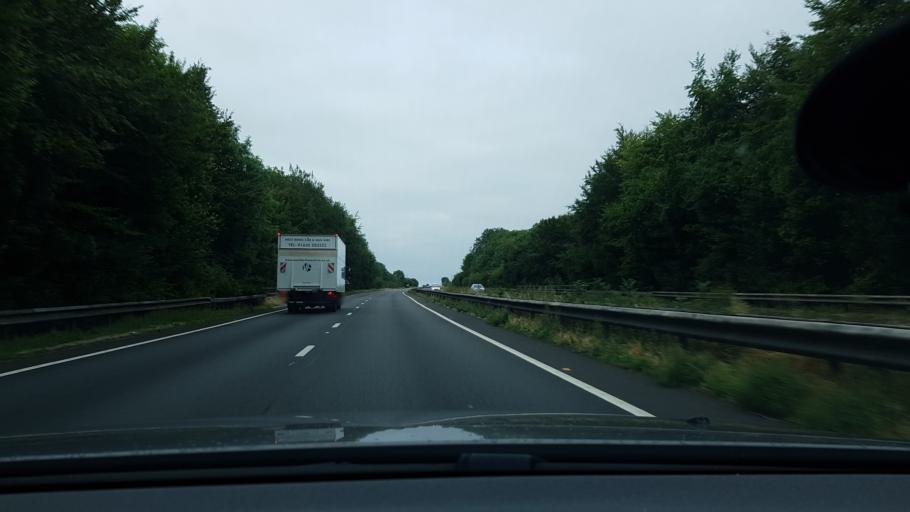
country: GB
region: England
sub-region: Hampshire
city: Overton
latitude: 51.2188
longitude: -1.3424
